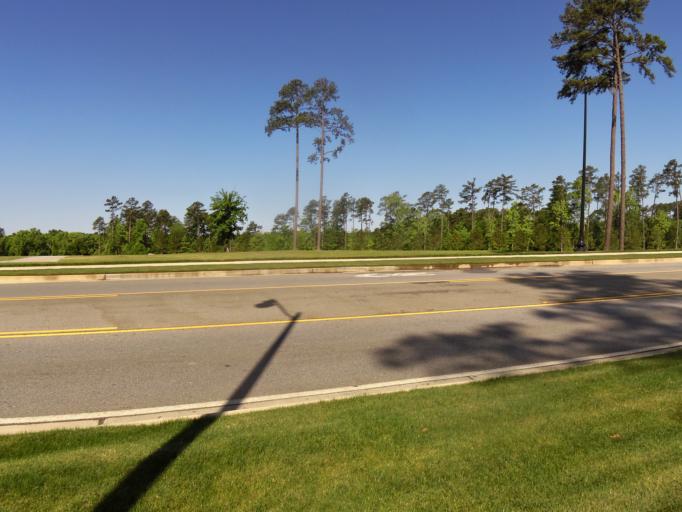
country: US
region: Georgia
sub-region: Columbia County
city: Martinez
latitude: 33.5042
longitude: -82.0318
